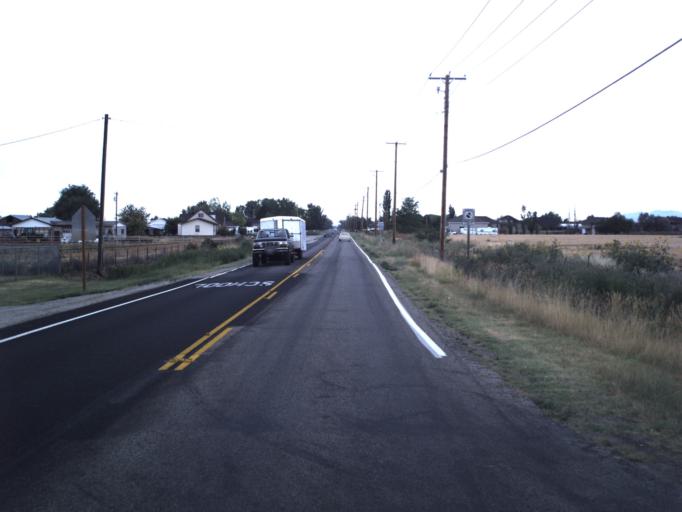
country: US
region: Utah
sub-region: Weber County
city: Hooper
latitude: 41.1639
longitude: -112.0933
